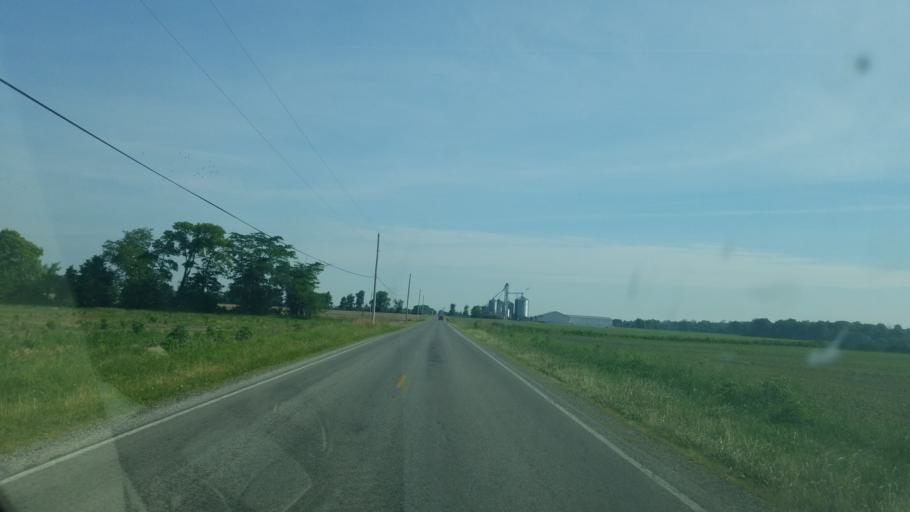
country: US
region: Ohio
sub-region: Hancock County
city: Findlay
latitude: 40.9716
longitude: -83.6986
